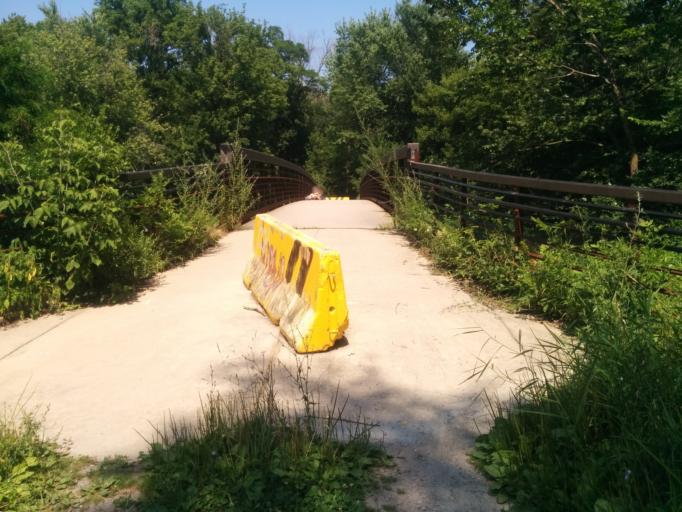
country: US
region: Illinois
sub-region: Cook County
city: River Grove
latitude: 41.9111
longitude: -87.8338
